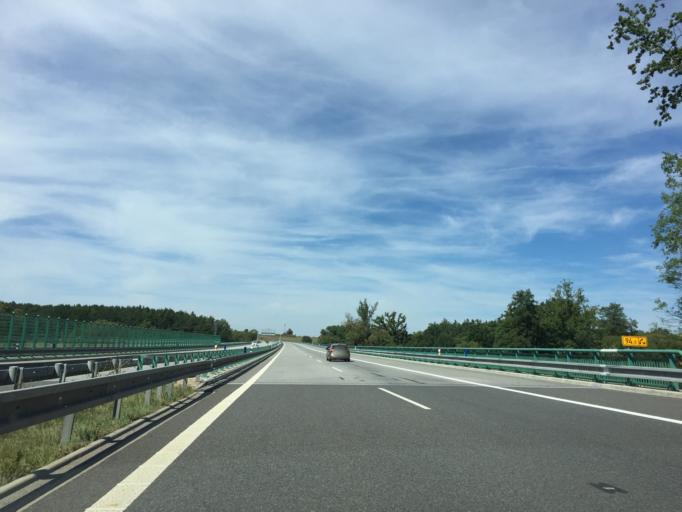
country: CZ
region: Jihocesky
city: Sobeslav
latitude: 49.2736
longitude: 14.7368
